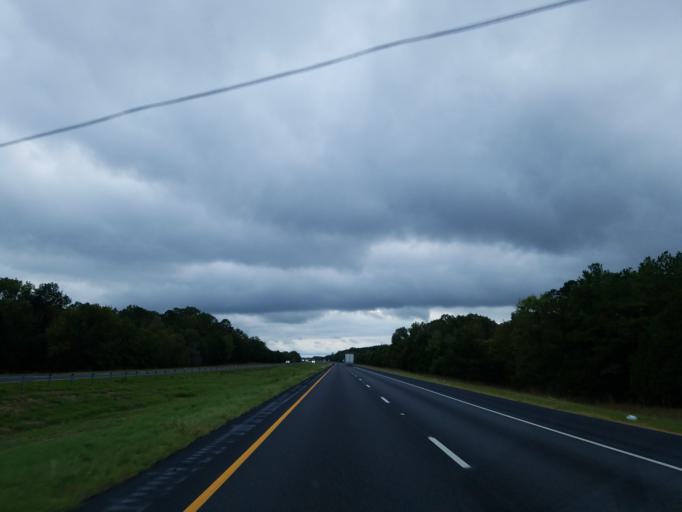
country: US
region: Alabama
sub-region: Sumter County
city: Livingston
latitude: 32.7144
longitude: -88.1277
